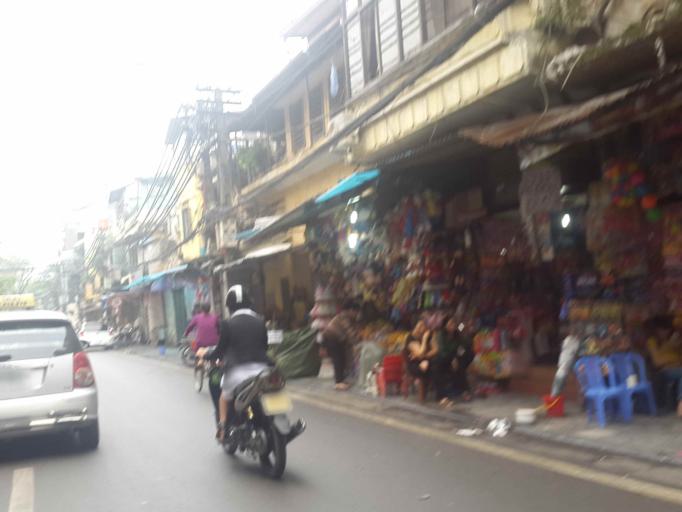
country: VN
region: Ha Noi
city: Hoan Kiem
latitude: 21.0367
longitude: 105.8487
